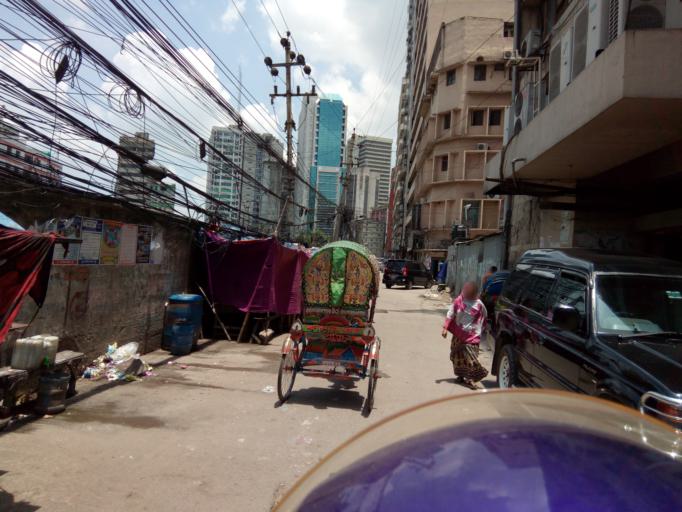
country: BD
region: Dhaka
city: Paltan
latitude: 23.7286
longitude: 90.4191
